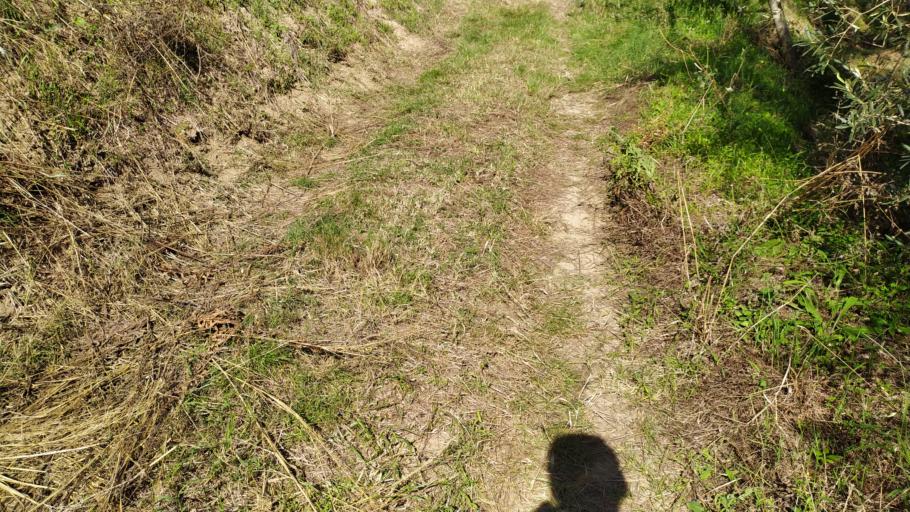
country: IT
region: Sicily
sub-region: Messina
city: Gualtieri Sicamino
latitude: 38.1590
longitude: 15.2977
